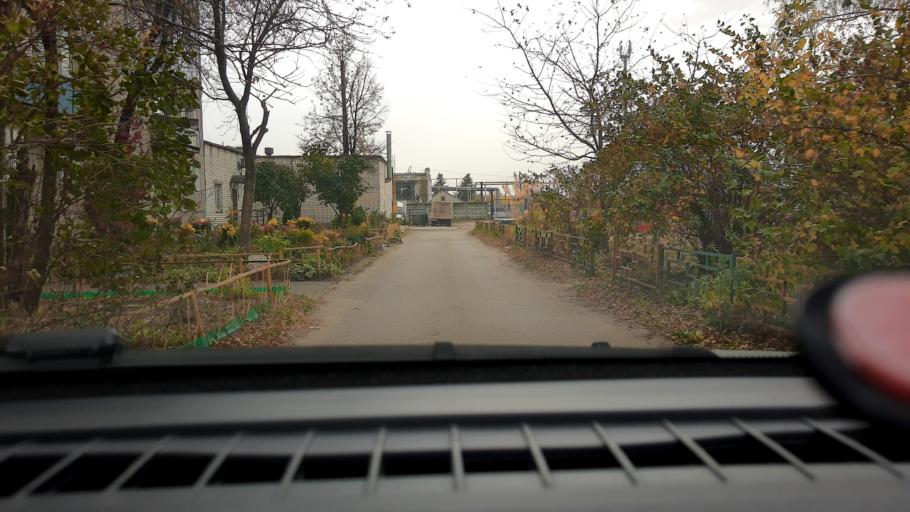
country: RU
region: Nizjnij Novgorod
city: Gorbatovka
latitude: 56.3102
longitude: 43.8094
